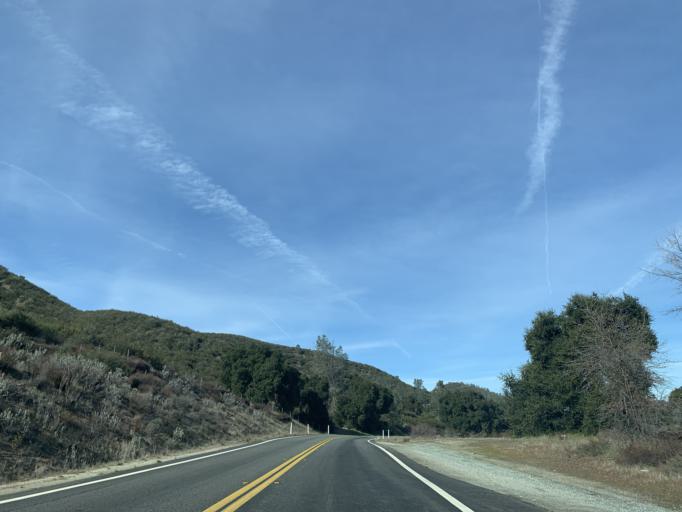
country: US
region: California
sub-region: Monterey County
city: Soledad
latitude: 36.5372
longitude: -121.1508
